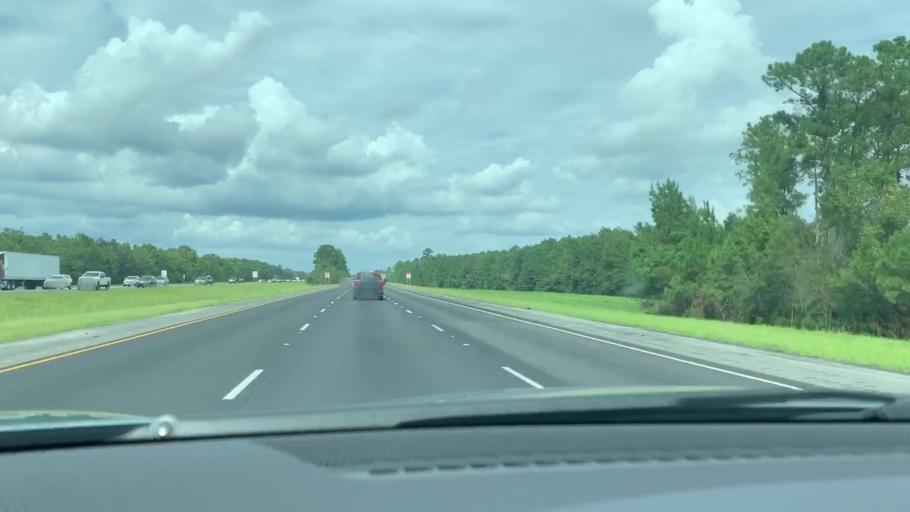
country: US
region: Georgia
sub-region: Liberty County
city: Midway
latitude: 31.7423
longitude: -81.3856
